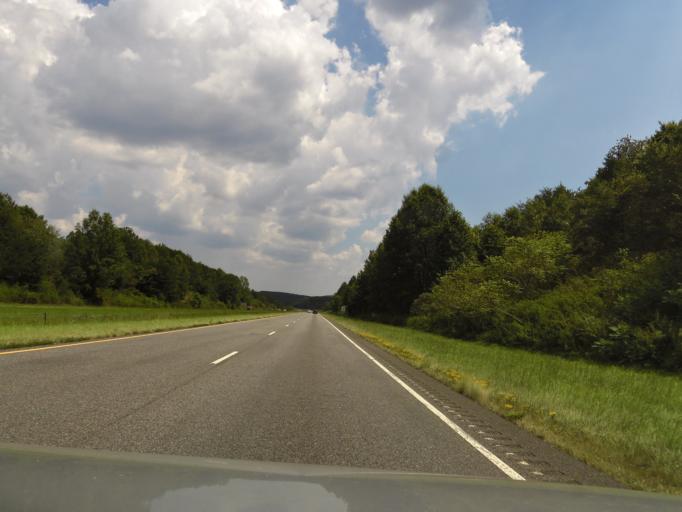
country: US
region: North Carolina
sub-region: Rutherford County
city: Rutherfordton
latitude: 35.2856
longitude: -82.0554
